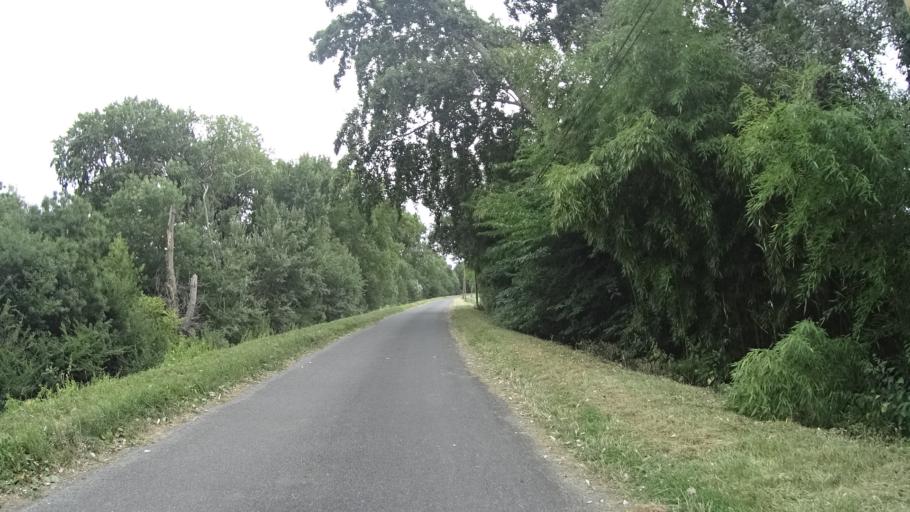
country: FR
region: Centre
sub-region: Departement d'Indre-et-Loire
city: Huismes
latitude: 47.2603
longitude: 0.2780
